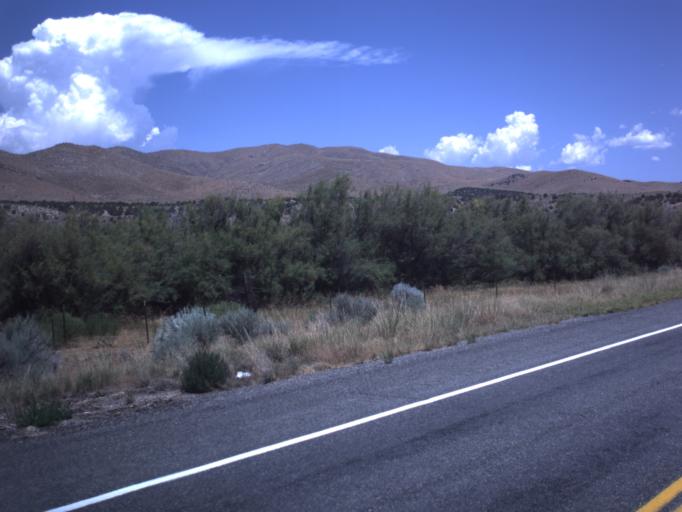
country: US
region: Utah
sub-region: Juab County
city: Nephi
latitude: 39.5830
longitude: -112.1705
